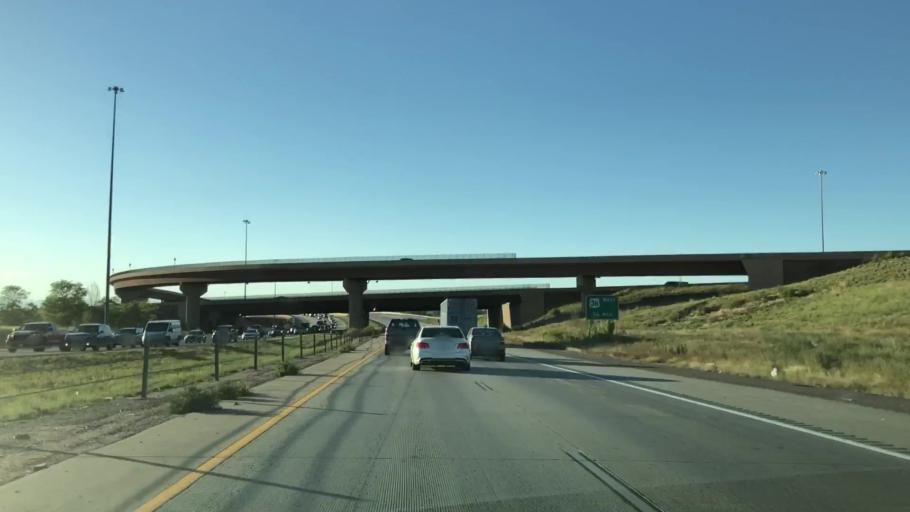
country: US
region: Colorado
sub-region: Adams County
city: Welby
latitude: 39.8224
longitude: -104.9622
